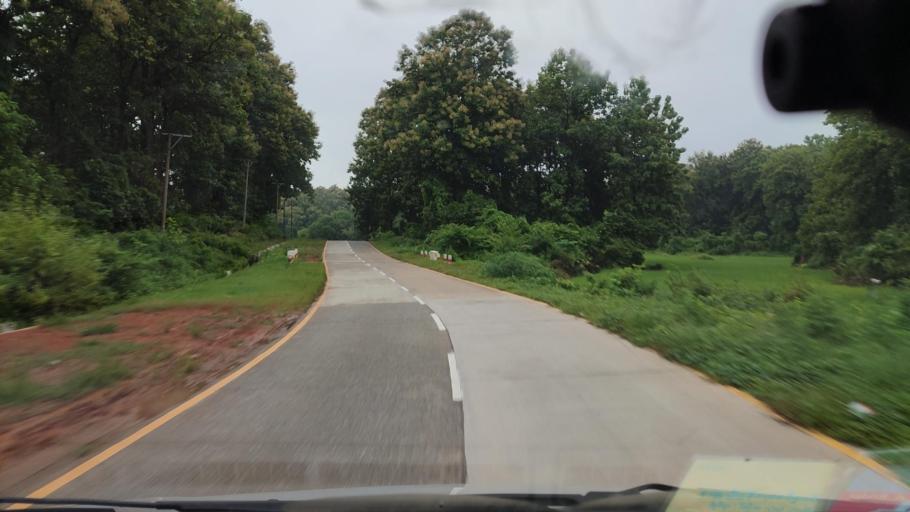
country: MM
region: Bago
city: Taungoo
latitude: 18.9876
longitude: 96.5179
